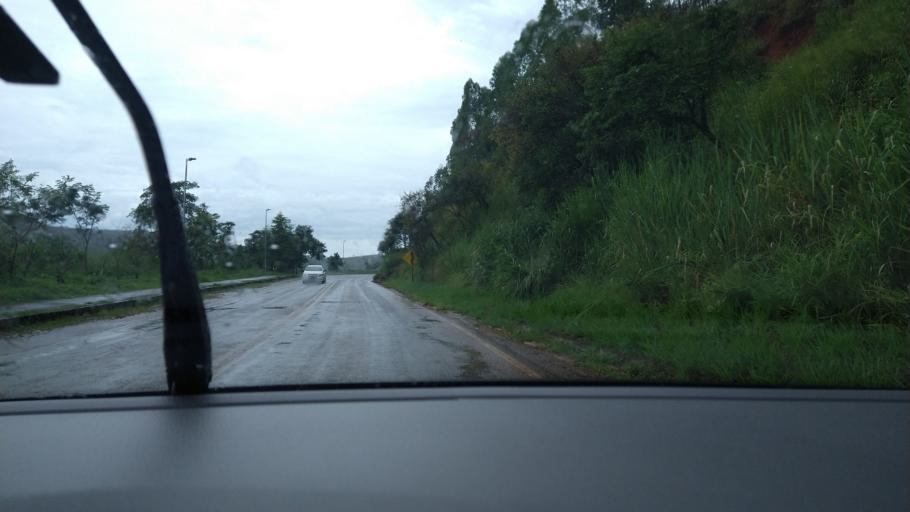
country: BR
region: Minas Gerais
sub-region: Ponte Nova
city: Ponte Nova
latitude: -20.3923
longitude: -42.9014
